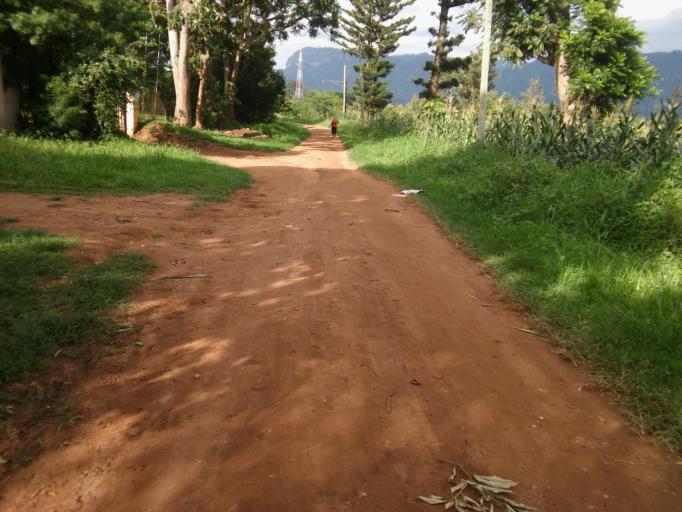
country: UG
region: Eastern Region
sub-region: Mbale District
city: Mbale
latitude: 1.0655
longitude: 34.1839
